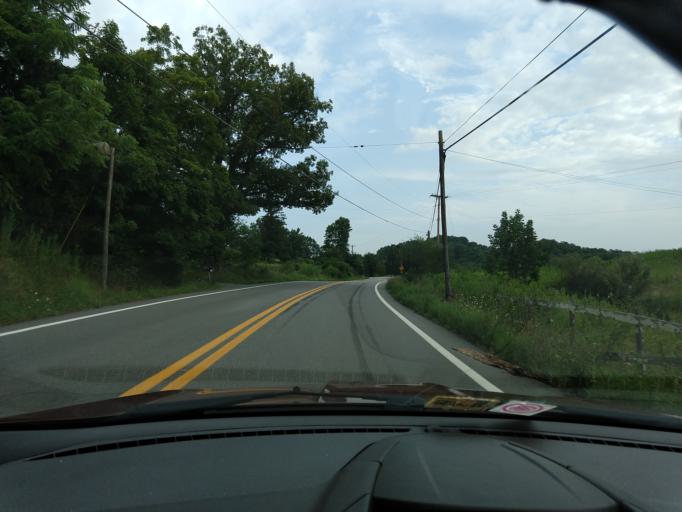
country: US
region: West Virginia
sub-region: Greenbrier County
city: Rainelle
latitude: 37.9397
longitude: -80.6512
